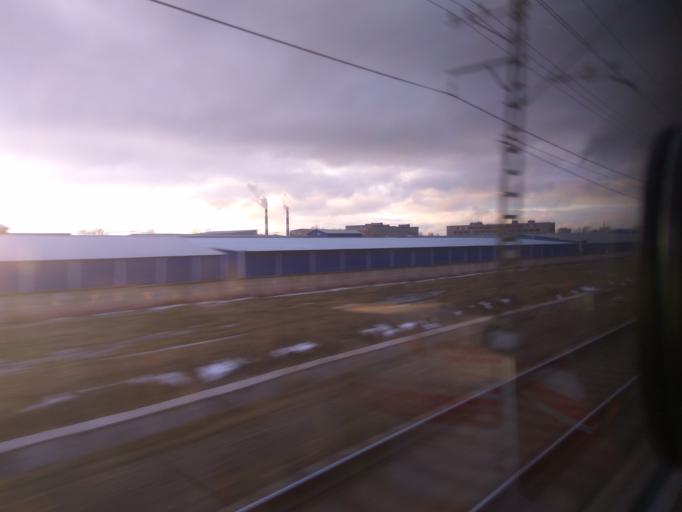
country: RU
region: St.-Petersburg
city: Kupchino
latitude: 59.8879
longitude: 30.3968
